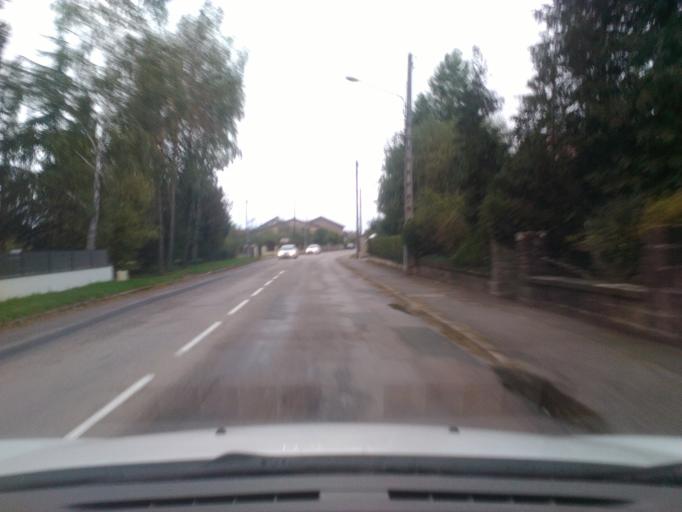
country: FR
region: Lorraine
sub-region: Departement des Vosges
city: Jeanmenil
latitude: 48.3346
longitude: 6.6963
